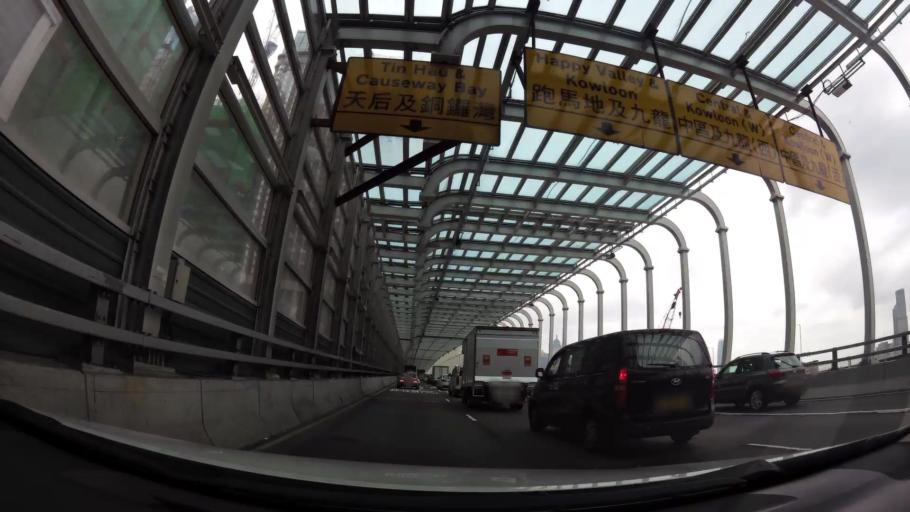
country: HK
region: Wanchai
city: Wan Chai
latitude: 22.2895
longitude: 114.1916
